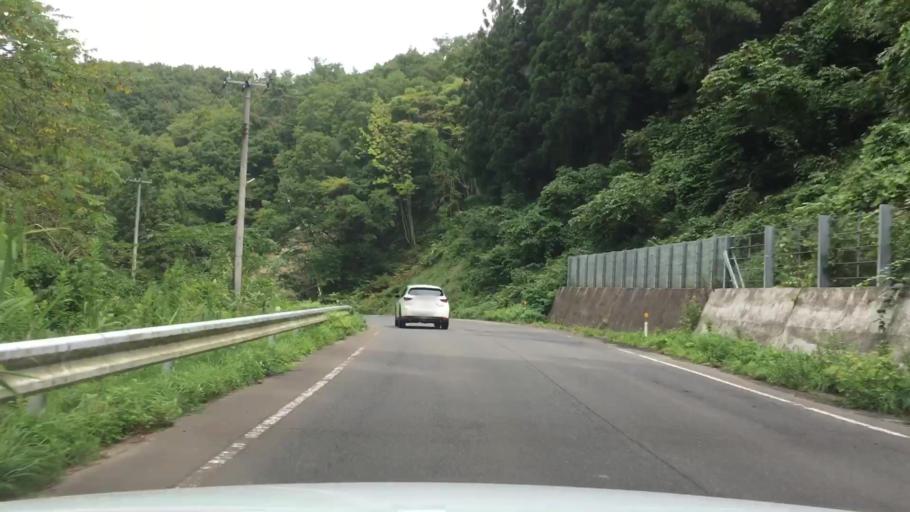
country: JP
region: Aomori
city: Shimokizukuri
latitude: 40.7348
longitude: 140.2499
